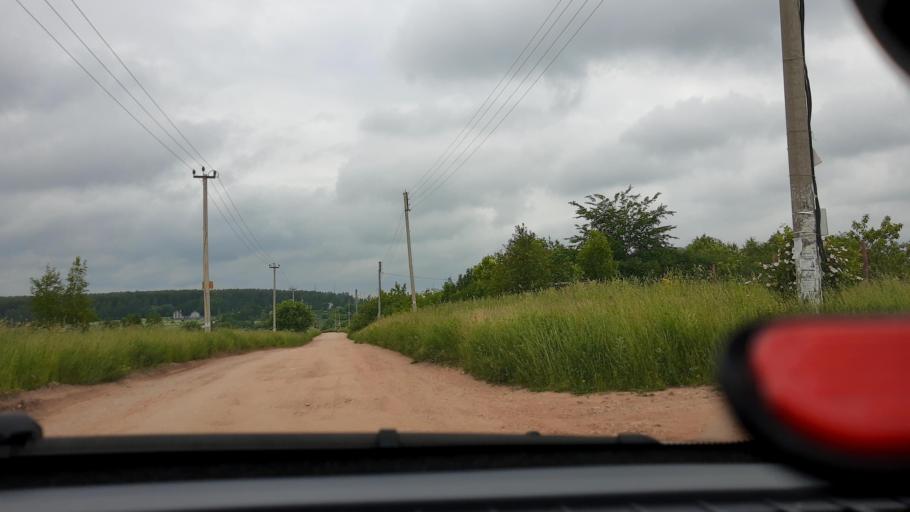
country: RU
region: Nizjnij Novgorod
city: Burevestnik
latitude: 56.1028
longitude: 43.9363
